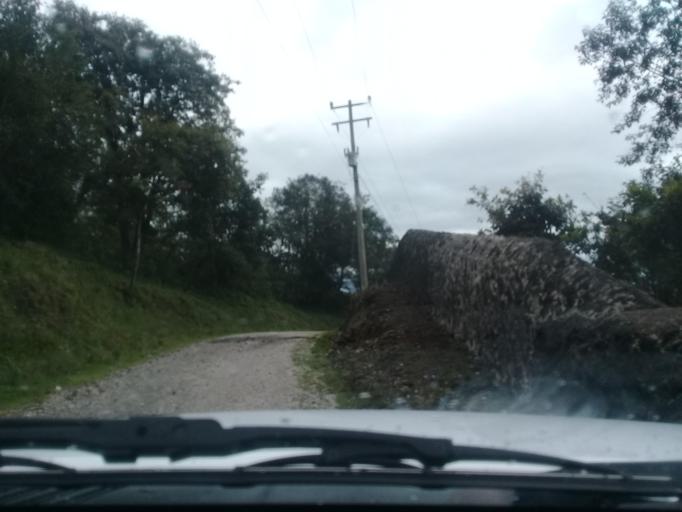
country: MX
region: Veracruz
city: Rafael Lucio
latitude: 19.6228
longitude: -96.9960
